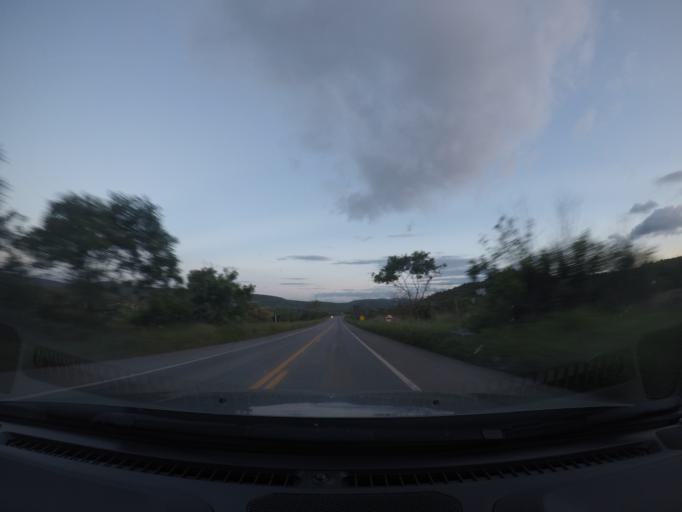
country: BR
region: Bahia
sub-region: Seabra
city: Seabra
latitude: -12.4283
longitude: -41.7606
